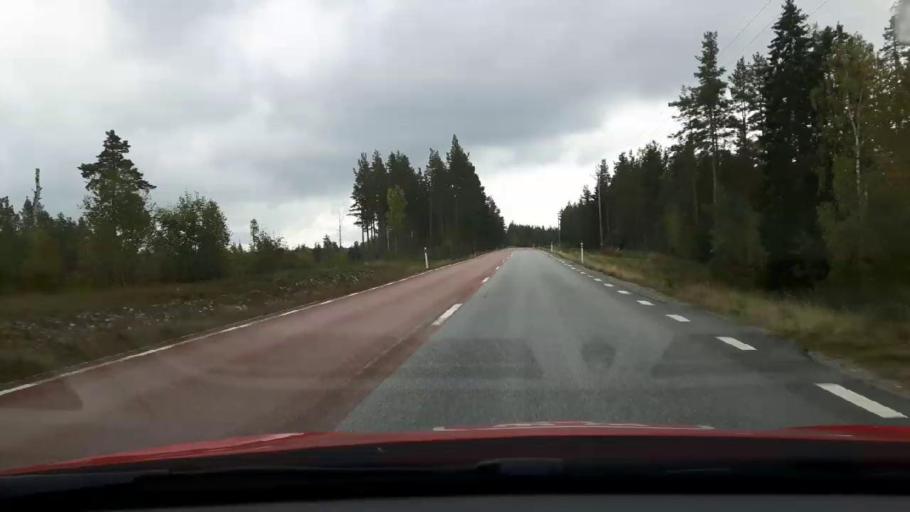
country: SE
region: Gaevleborg
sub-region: Soderhamns Kommun
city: Soderhamn
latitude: 61.1270
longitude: 16.9297
